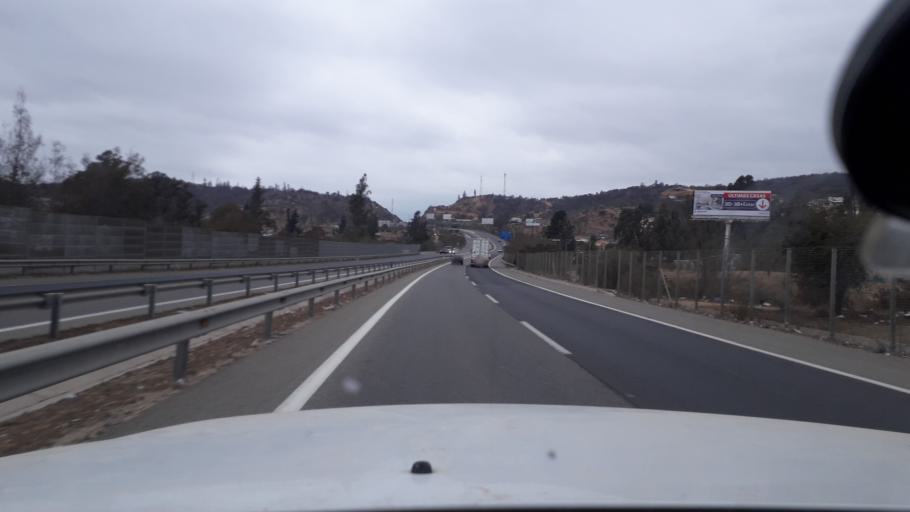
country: CL
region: Valparaiso
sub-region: Provincia de Marga Marga
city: Villa Alemana
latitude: -33.0568
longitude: -71.3394
